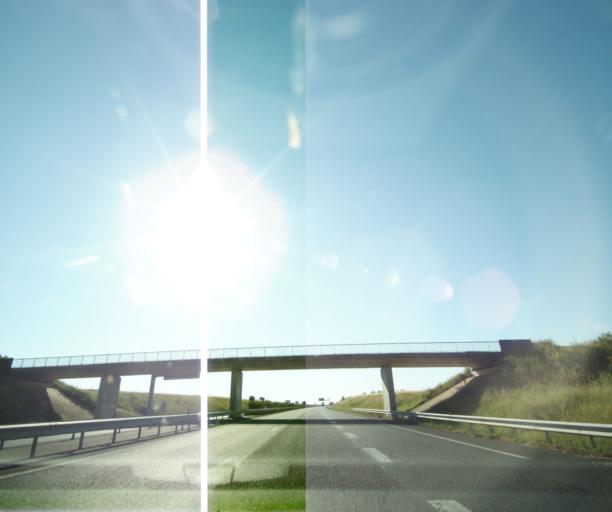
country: FR
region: Bourgogne
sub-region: Departement de l'Yonne
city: Thorigny-sur-Oreuse
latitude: 48.2446
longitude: 3.5634
